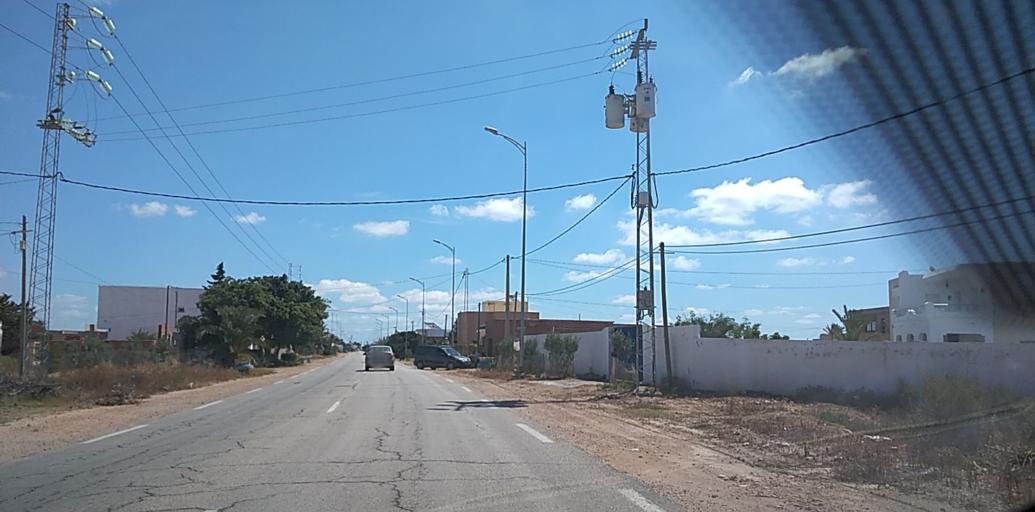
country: TN
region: Safaqis
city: Al Qarmadah
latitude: 34.6662
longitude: 11.1305
